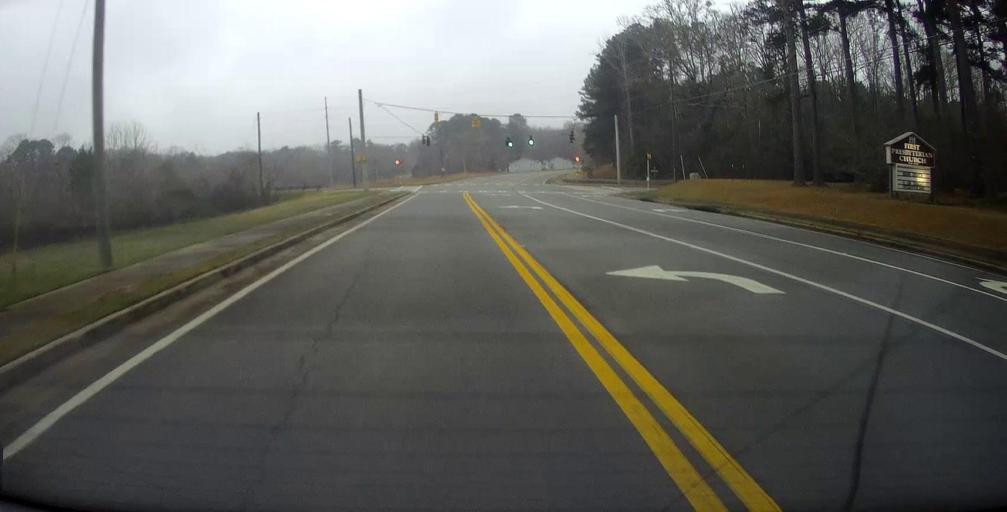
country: US
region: Georgia
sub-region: Spalding County
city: East Griffin
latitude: 33.2230
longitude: -84.2410
